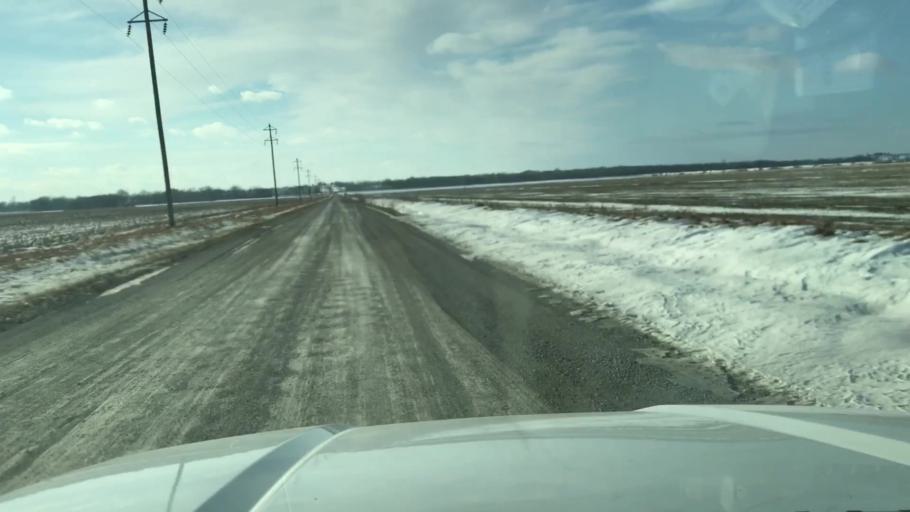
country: US
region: Missouri
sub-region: Holt County
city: Oregon
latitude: 40.1300
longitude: -95.0229
